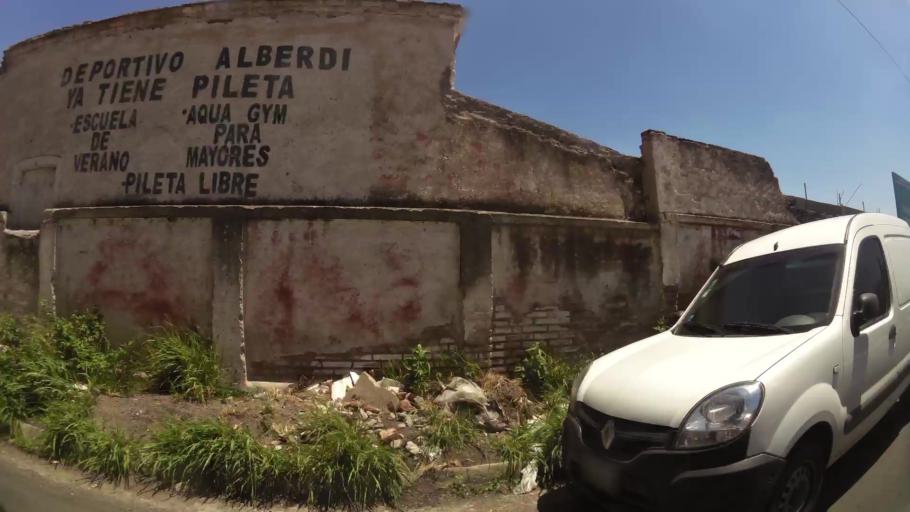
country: AR
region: Cordoba
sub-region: Departamento de Capital
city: Cordoba
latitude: -31.4009
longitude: -64.2060
